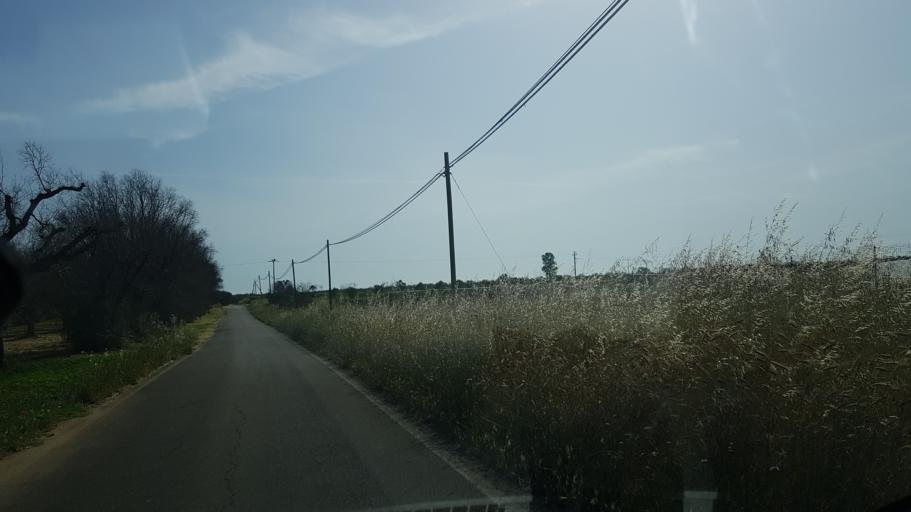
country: IT
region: Apulia
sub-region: Provincia di Brindisi
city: Torchiarolo
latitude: 40.5109
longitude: 18.0746
